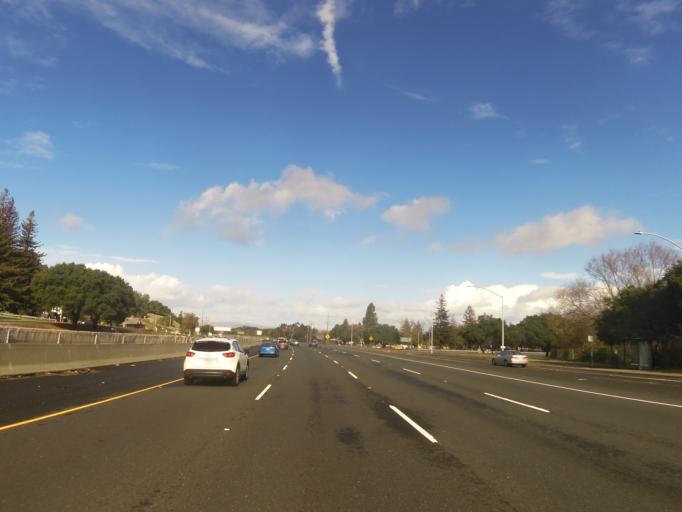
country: US
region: California
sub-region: Marin County
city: Lucas Valley-Marinwood
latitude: 38.0482
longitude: -122.5322
